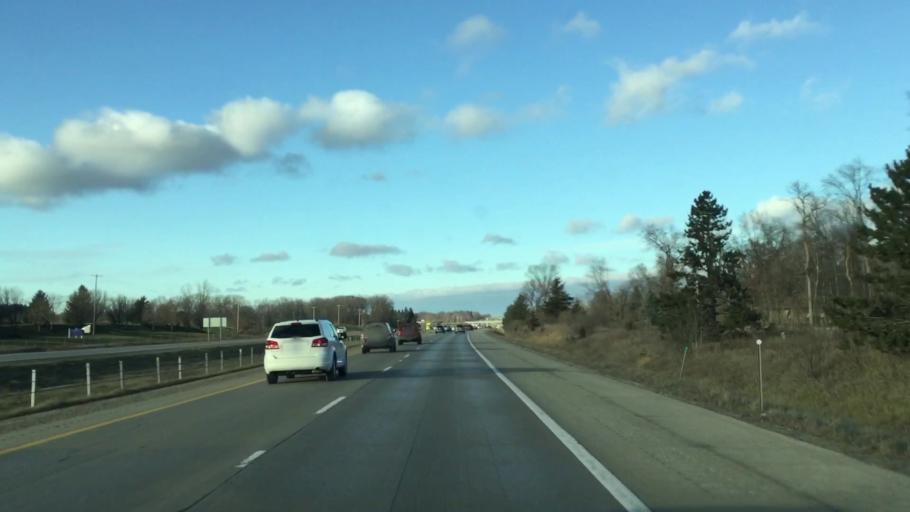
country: US
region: Michigan
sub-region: Genesee County
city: Fenton
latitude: 42.6953
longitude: -83.7609
